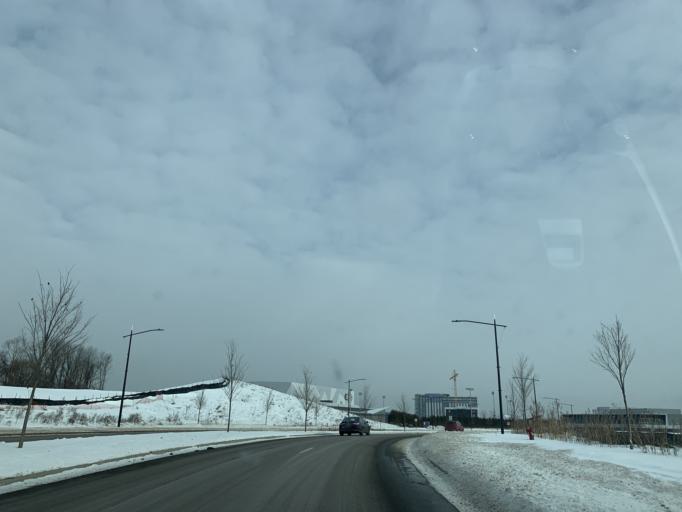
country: US
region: Minnesota
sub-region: Dakota County
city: Mendota Heights
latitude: 44.8589
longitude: -93.1225
